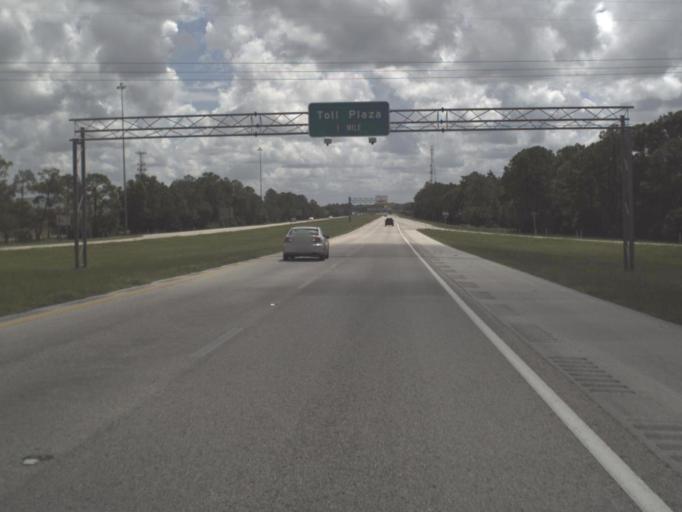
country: US
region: Florida
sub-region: Collier County
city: Golden Gate
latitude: 26.1593
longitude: -81.6834
